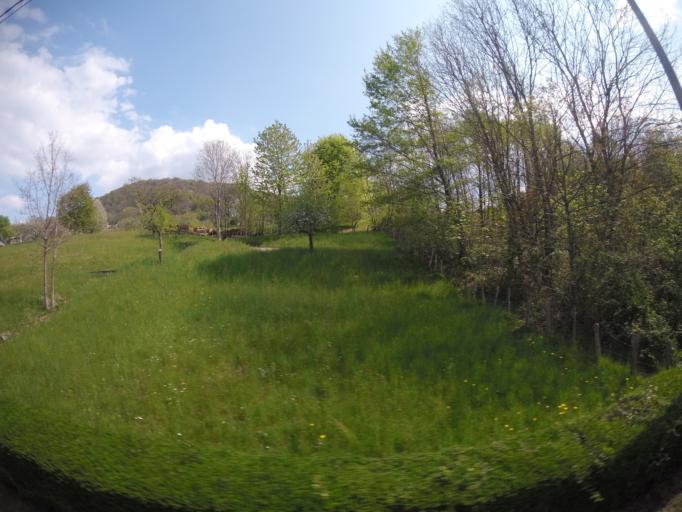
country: IT
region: Piedmont
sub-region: Provincia di Novara
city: Pettenasco
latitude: 45.8249
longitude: 8.4002
